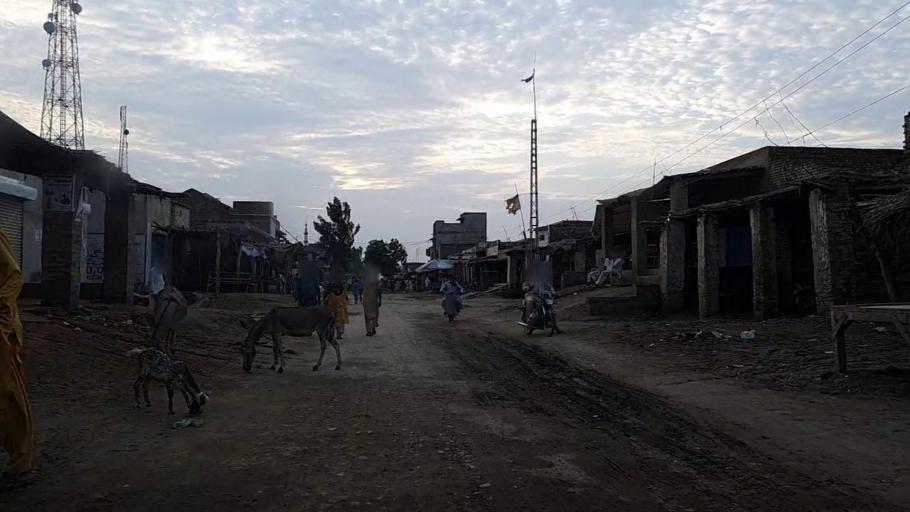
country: PK
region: Sindh
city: Naushahro Firoz
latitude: 26.8102
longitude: 68.1982
